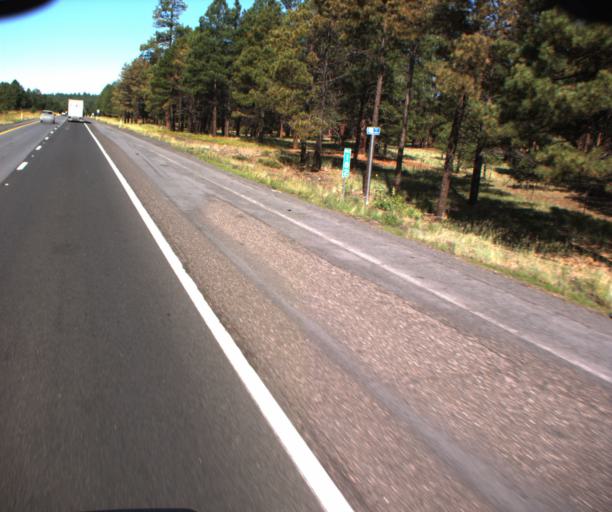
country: US
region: Arizona
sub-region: Coconino County
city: Parks
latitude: 35.2486
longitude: -111.8746
